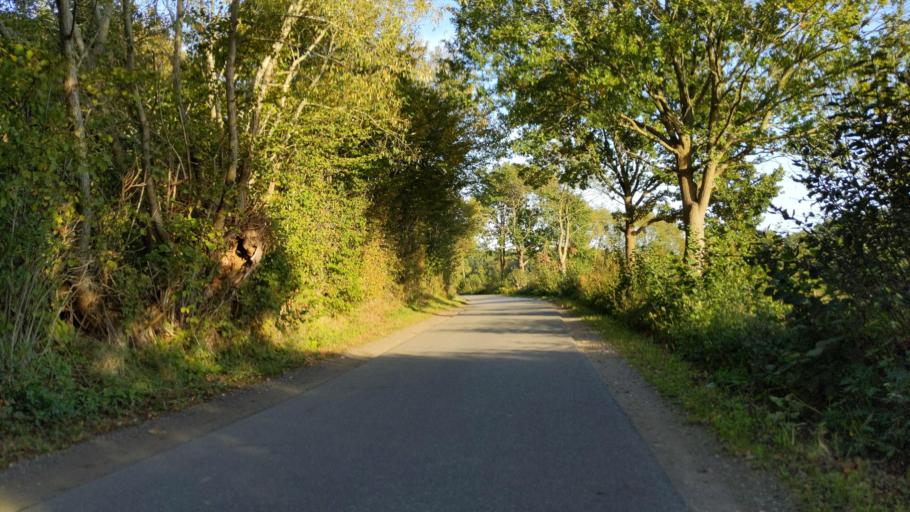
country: DE
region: Schleswig-Holstein
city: Susel
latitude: 54.0873
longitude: 10.6563
